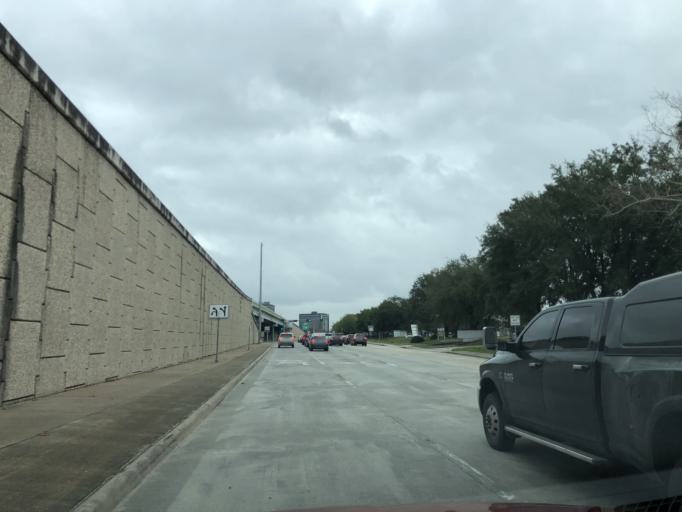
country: US
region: Texas
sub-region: Harris County
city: Aldine
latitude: 29.9402
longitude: -95.4092
